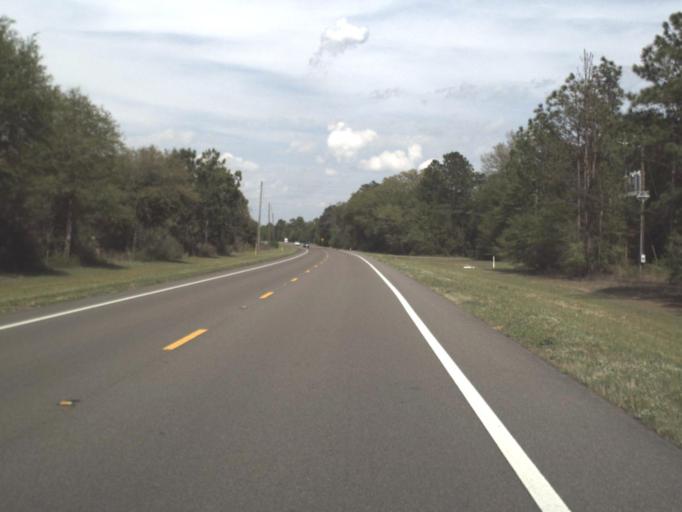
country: US
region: Florida
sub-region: Santa Rosa County
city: East Milton
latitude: 30.6528
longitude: -86.8936
